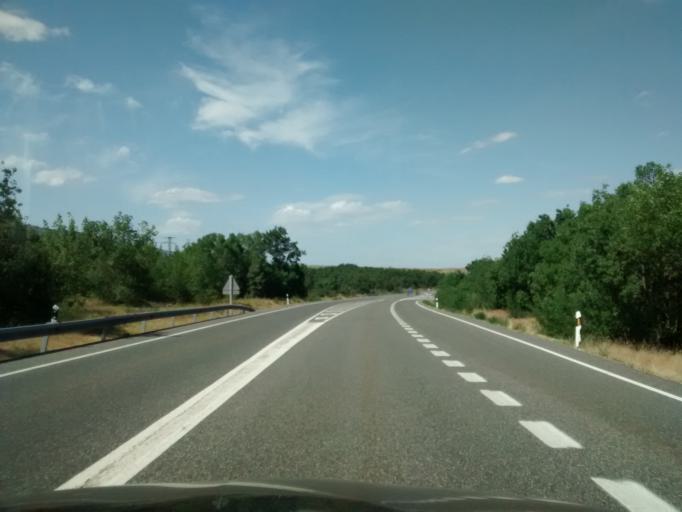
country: ES
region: Castille and Leon
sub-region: Provincia de Segovia
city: Sotosalbos
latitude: 41.0319
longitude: -3.9355
